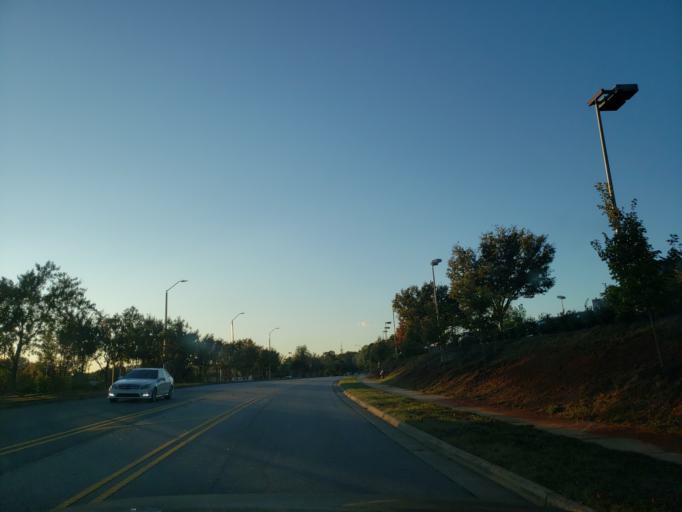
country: US
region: North Carolina
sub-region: Wake County
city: Apex
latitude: 35.7390
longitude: -78.8122
